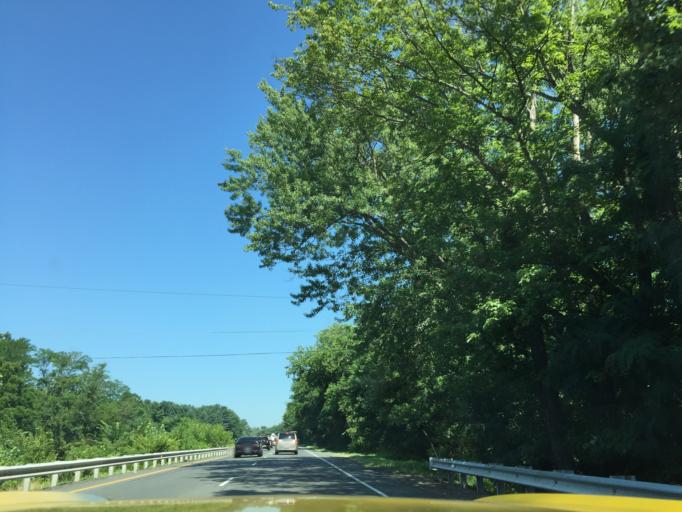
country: US
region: Virginia
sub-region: Fairfax County
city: Great Falls
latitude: 38.9714
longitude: -77.2991
